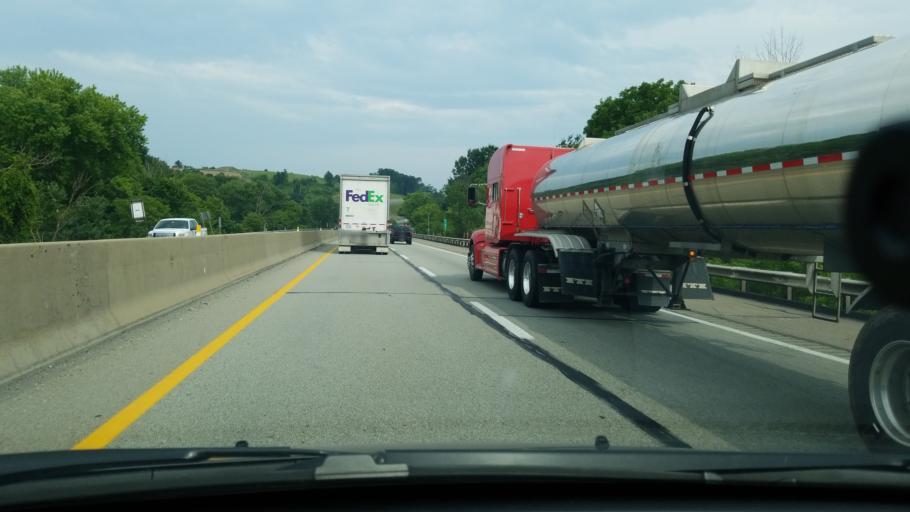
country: US
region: Pennsylvania
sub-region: Beaver County
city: Big Beaver
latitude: 40.8194
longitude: -80.3380
